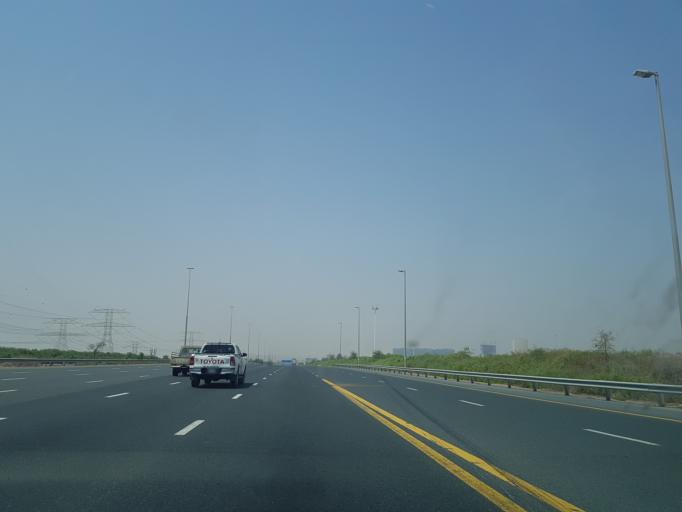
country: AE
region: Ash Shariqah
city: Sharjah
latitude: 25.1019
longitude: 55.4129
